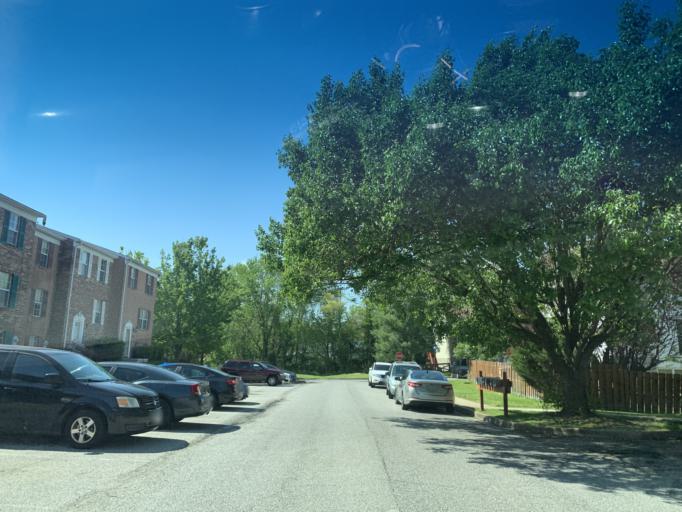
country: US
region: Maryland
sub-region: Harford County
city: Edgewood
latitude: 39.4414
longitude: -76.2881
